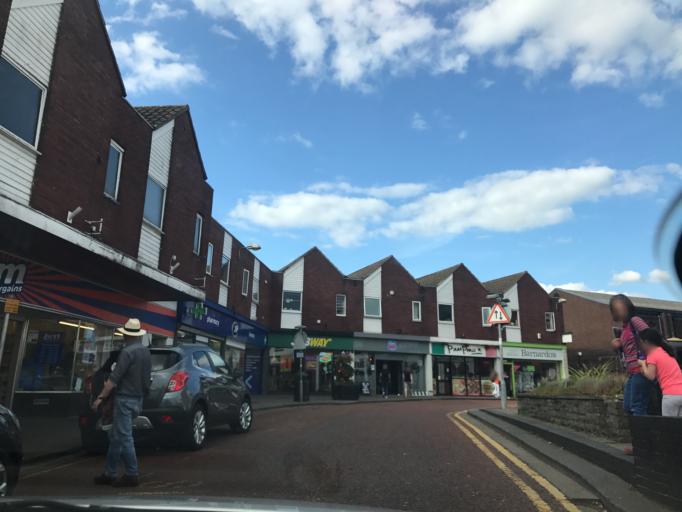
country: GB
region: England
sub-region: Cheshire East
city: Nantwich
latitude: 53.0679
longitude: -2.5234
